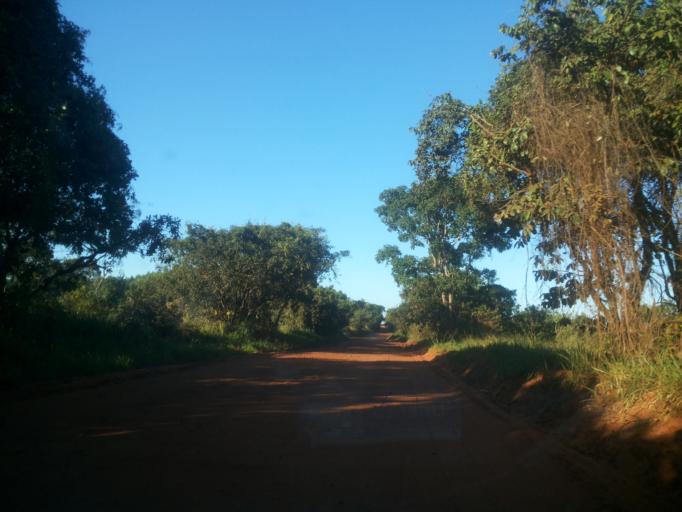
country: BR
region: Minas Gerais
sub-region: Campina Verde
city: Campina Verde
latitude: -19.3086
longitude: -49.7572
